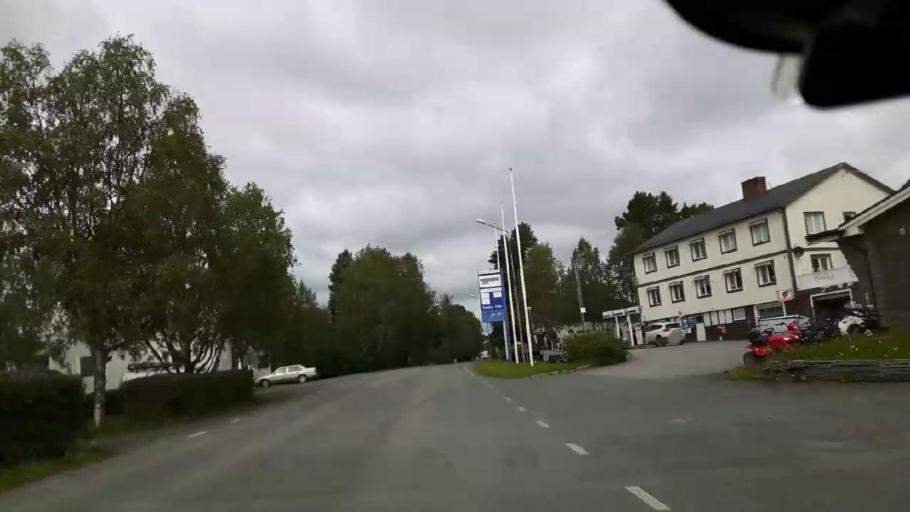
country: SE
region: Jaemtland
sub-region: Krokoms Kommun
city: Valla
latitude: 63.4953
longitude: 13.8992
